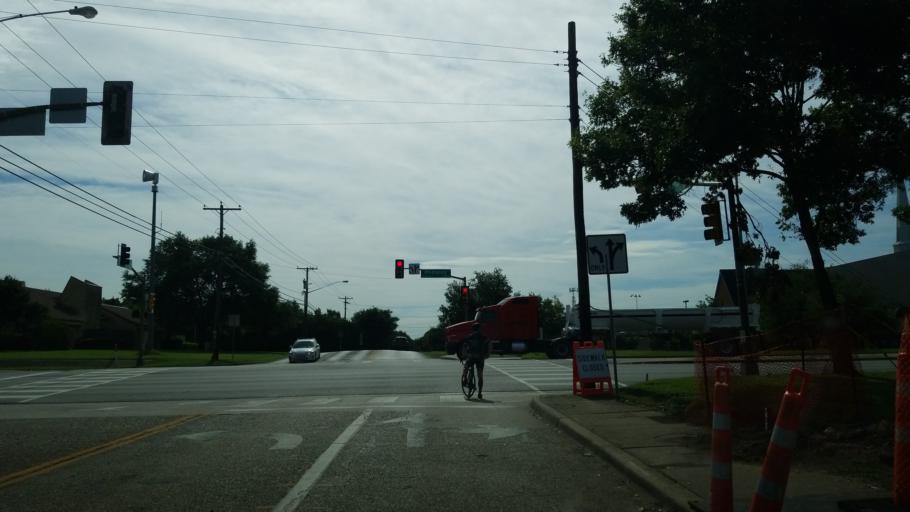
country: US
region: Texas
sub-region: Dallas County
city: Addison
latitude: 32.9022
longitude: -96.8386
